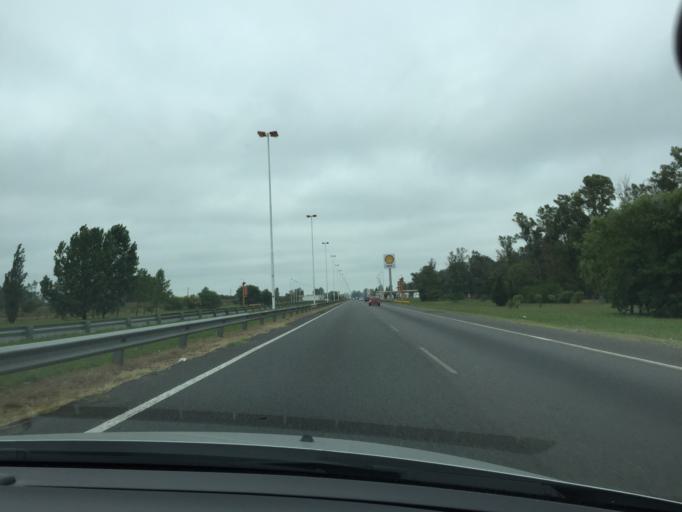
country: AR
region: Buenos Aires
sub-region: Partido de Ezeiza
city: Ezeiza
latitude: -34.8580
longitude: -58.5596
